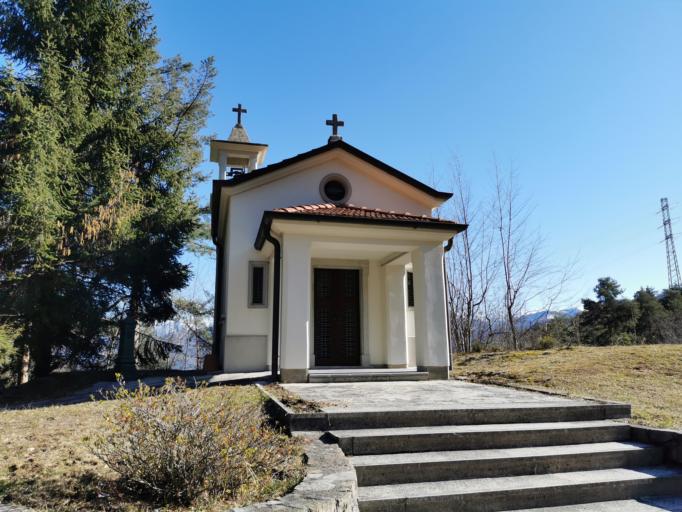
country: IT
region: Lombardy
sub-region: Provincia di Como
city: Grandola ed Uniti
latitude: 46.0142
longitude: 9.2203
